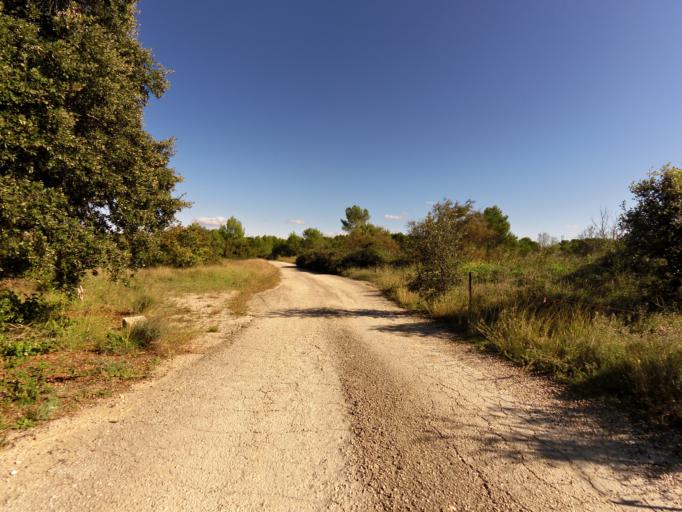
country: FR
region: Languedoc-Roussillon
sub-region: Departement de l'Herault
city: Villetelle
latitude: 43.7315
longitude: 4.1526
